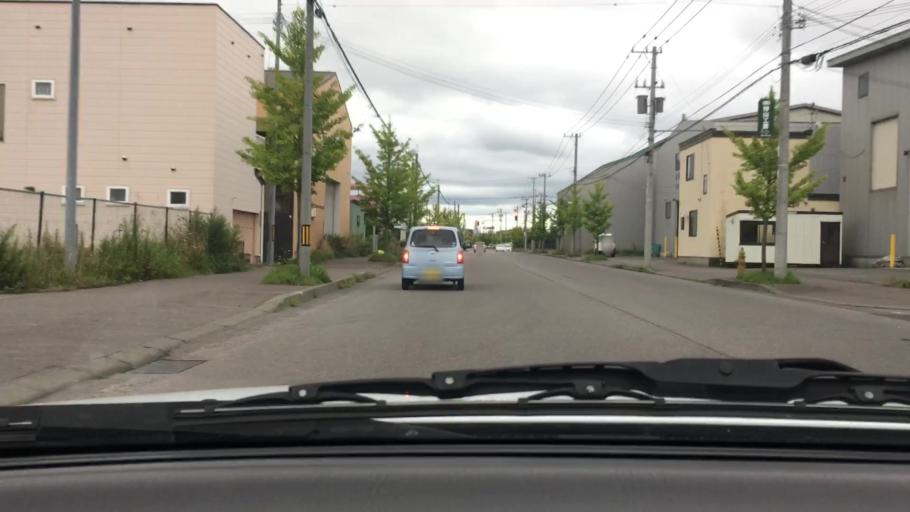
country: JP
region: Hokkaido
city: Hakodate
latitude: 41.7985
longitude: 140.7245
